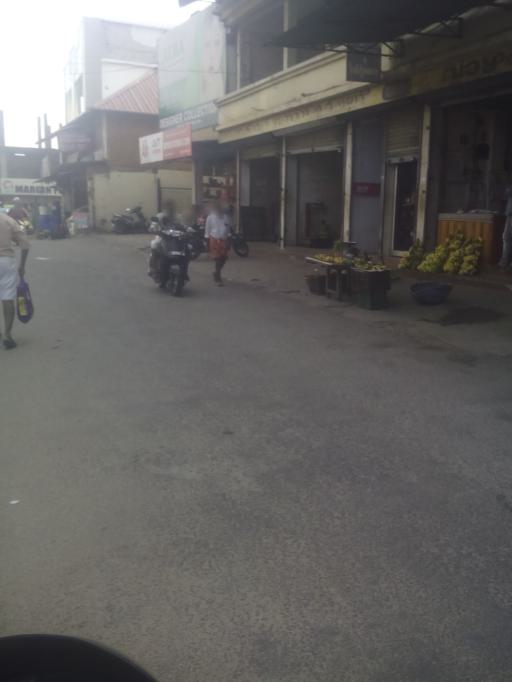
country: IN
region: Kerala
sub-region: Ernakulam
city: Perumpavur
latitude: 10.1155
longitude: 76.4788
